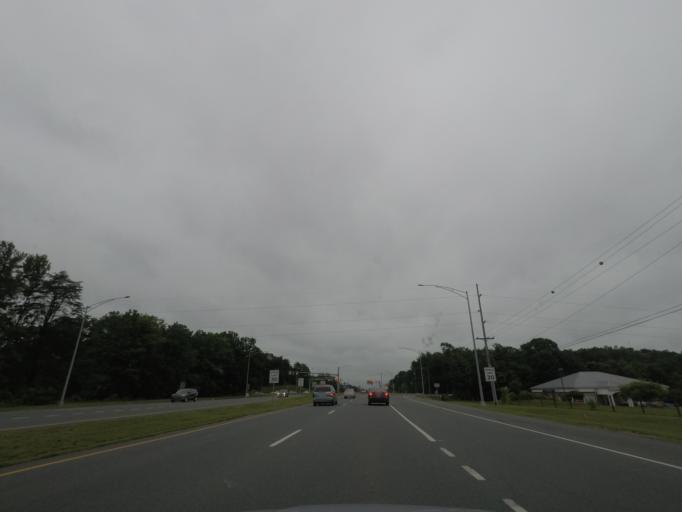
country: US
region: Virginia
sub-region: Fluvanna County
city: Palmyra
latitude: 37.9747
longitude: -78.2157
